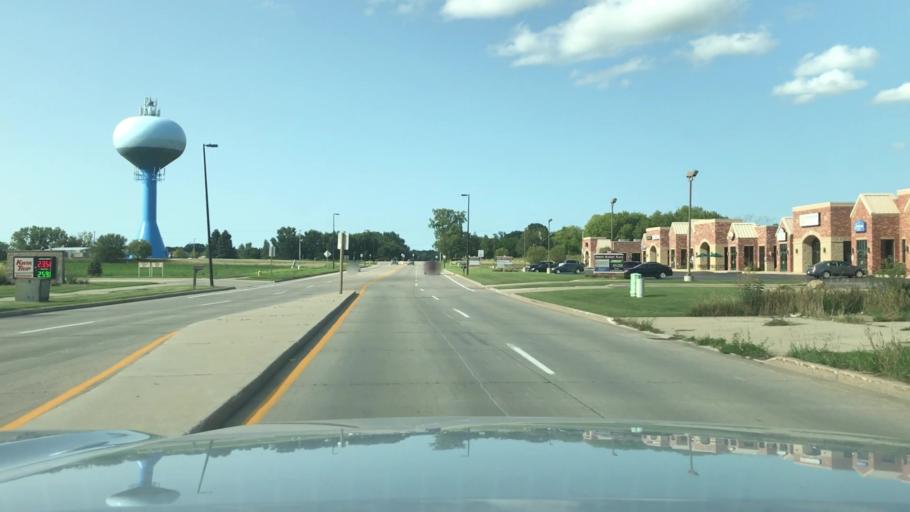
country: US
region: Wisconsin
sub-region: Brown County
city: Bellevue
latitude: 44.4850
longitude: -87.9177
